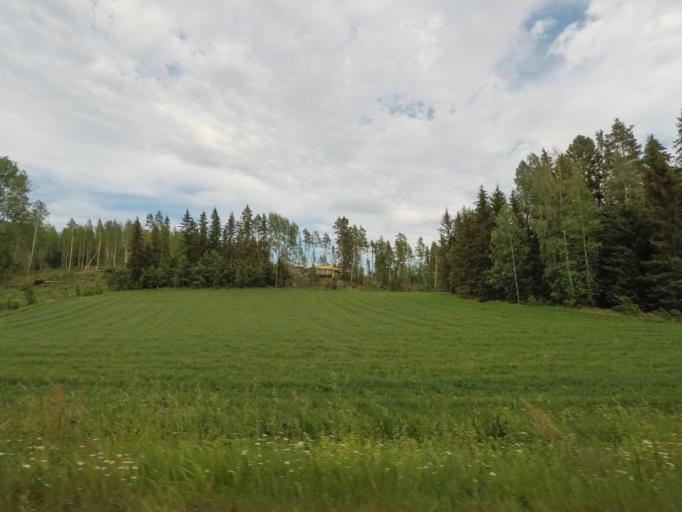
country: FI
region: Paijanne Tavastia
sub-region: Lahti
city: Hollola
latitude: 60.8665
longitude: 25.5014
